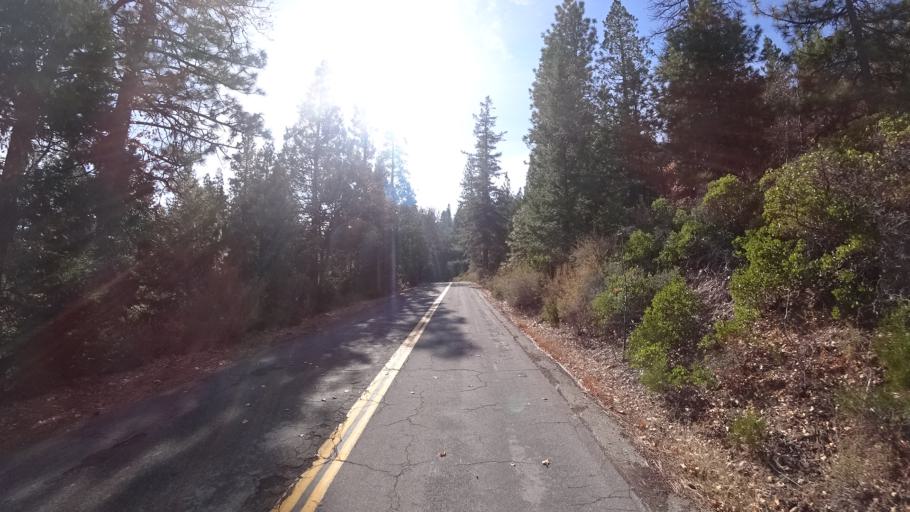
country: US
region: California
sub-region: Siskiyou County
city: Weed
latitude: 41.4290
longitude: -122.3985
